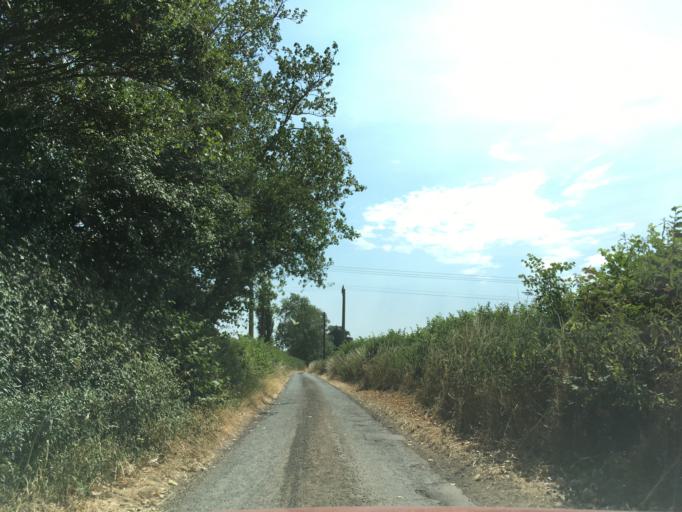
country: GB
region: England
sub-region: South Gloucestershire
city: Thornbury
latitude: 51.5940
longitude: -2.5173
